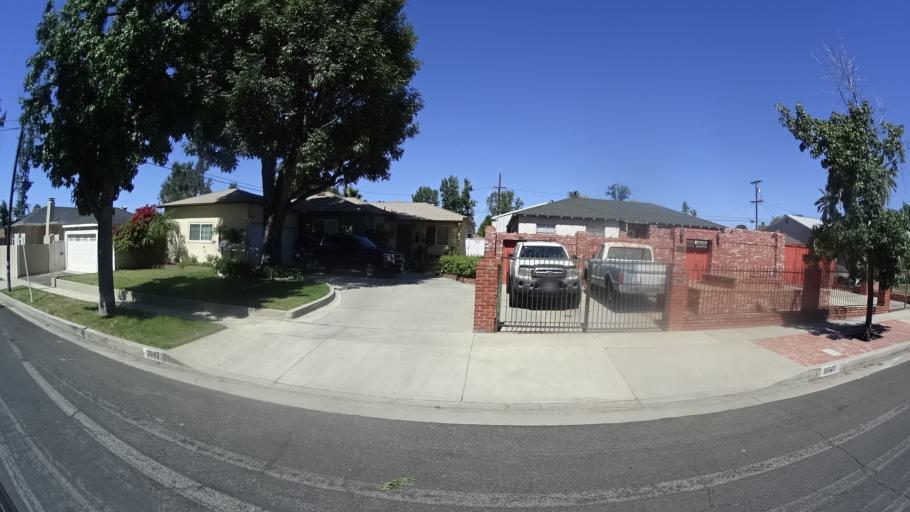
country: US
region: California
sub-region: Los Angeles County
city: San Fernando
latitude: 34.2513
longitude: -118.4610
